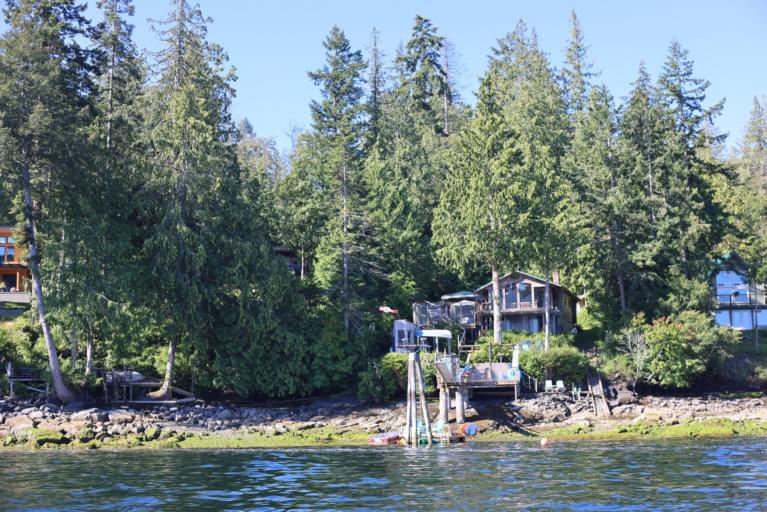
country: CA
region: British Columbia
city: North Cowichan
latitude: 48.8052
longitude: -123.5807
